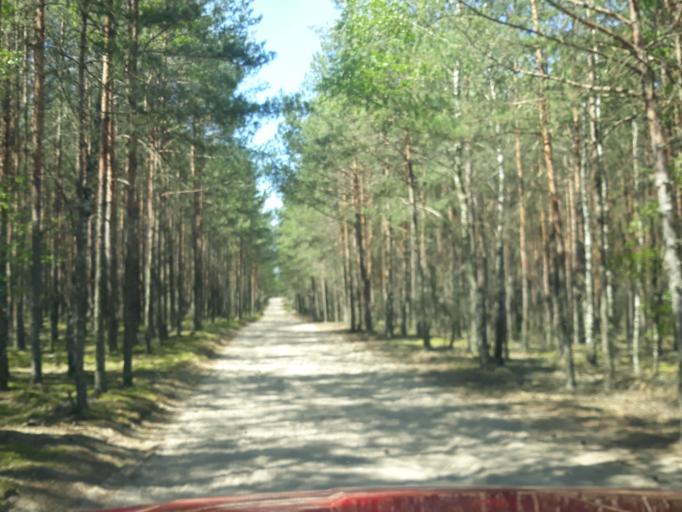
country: PL
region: Pomeranian Voivodeship
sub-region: Powiat chojnicki
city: Chojnice
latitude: 53.8669
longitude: 17.5379
